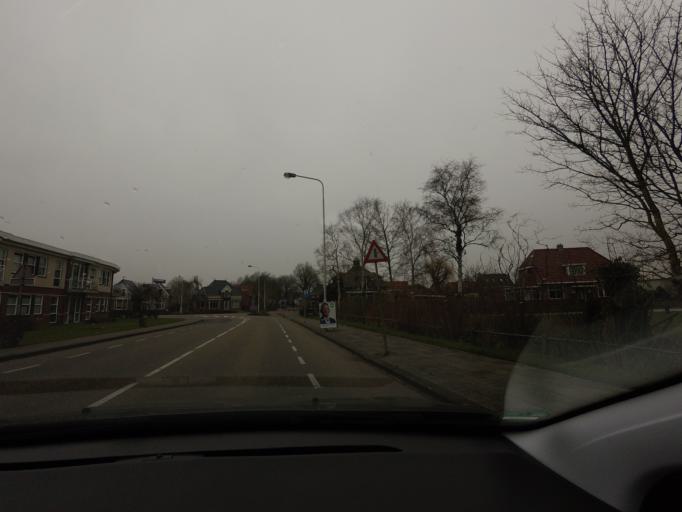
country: NL
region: Friesland
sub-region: Gemeente Franekeradeel
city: Franeker
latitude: 53.1827
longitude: 5.5519
